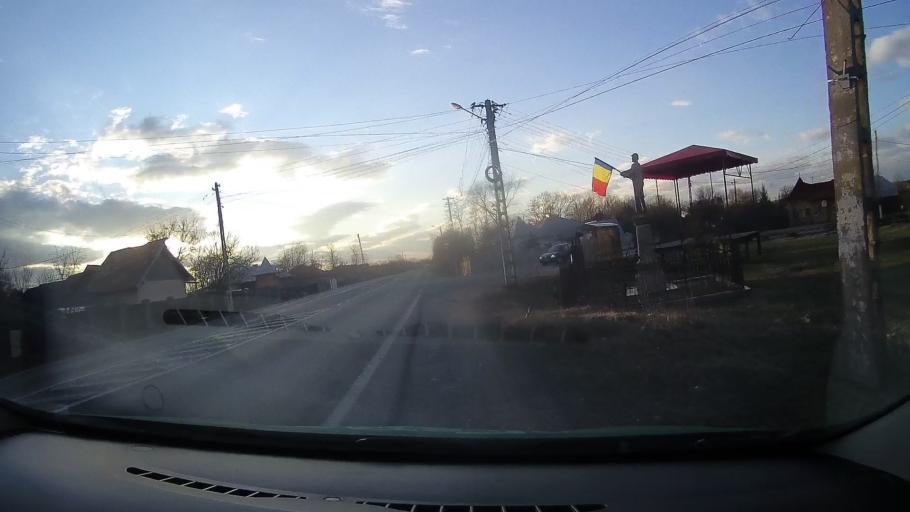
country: RO
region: Dambovita
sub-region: Comuna Gura Ocnitei
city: Adanca
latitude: 44.9104
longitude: 25.6166
